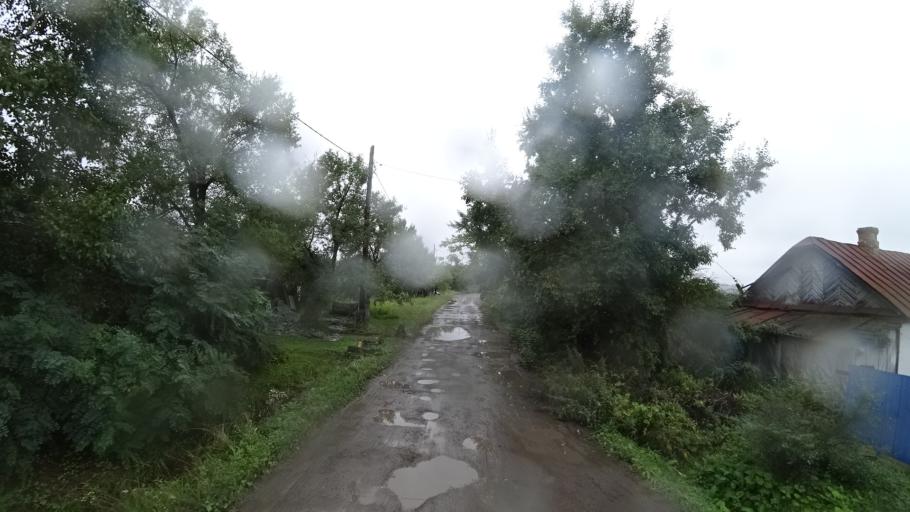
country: RU
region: Primorskiy
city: Monastyrishche
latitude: 44.2004
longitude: 132.4217
